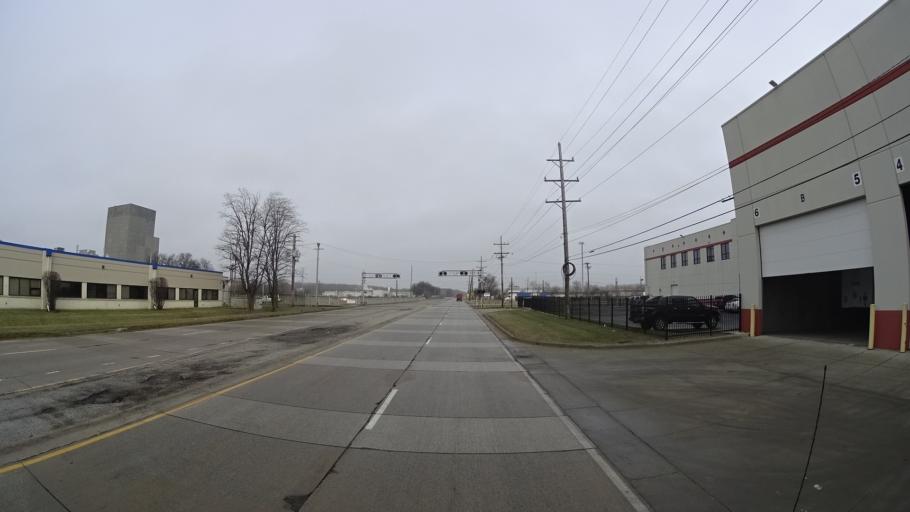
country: US
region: Illinois
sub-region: Cook County
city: Chicago Heights
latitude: 41.5216
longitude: -87.6163
